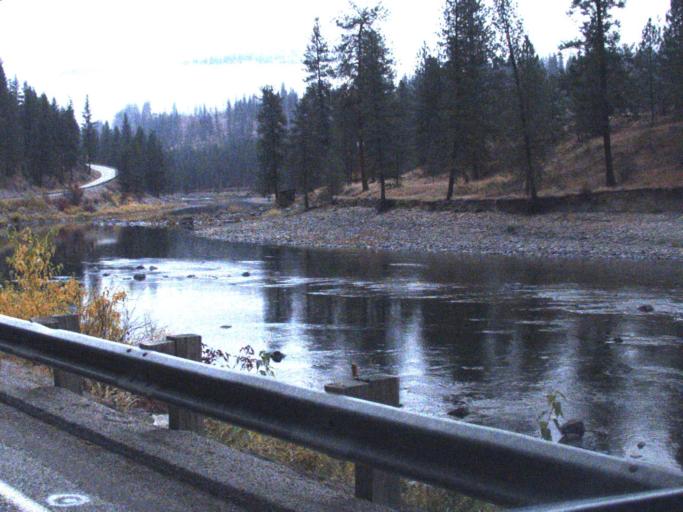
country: US
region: Washington
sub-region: Stevens County
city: Kettle Falls
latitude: 48.7935
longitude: -118.1612
